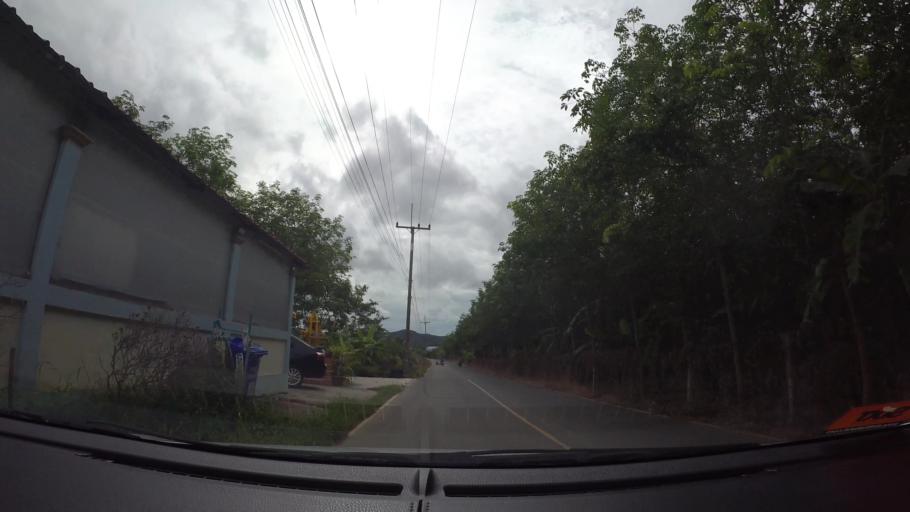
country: TH
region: Chon Buri
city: Sattahip
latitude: 12.7197
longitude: 100.9088
